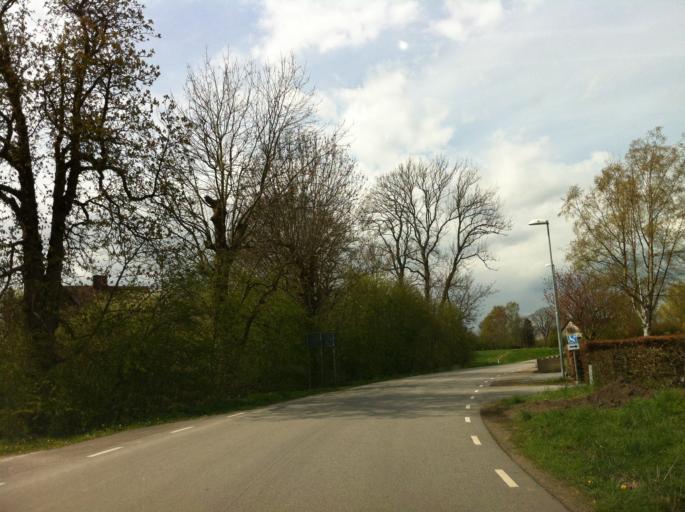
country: SE
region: Skane
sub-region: Kavlinge Kommun
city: Kaevlinge
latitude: 55.8039
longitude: 13.1535
